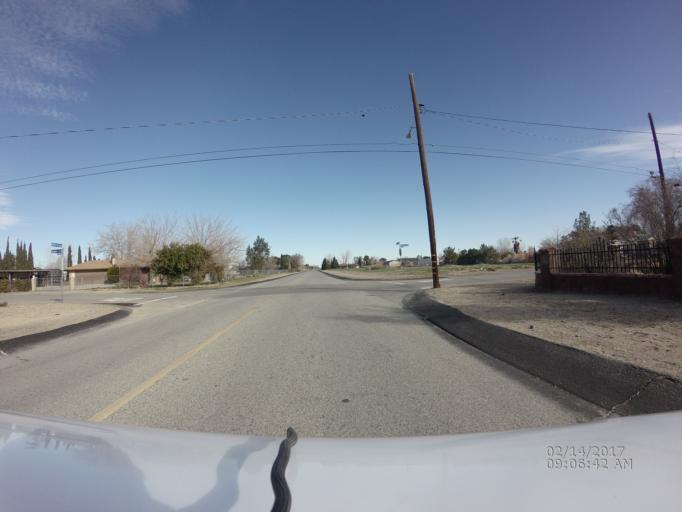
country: US
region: California
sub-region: Los Angeles County
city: Littlerock
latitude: 34.5687
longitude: -117.9432
